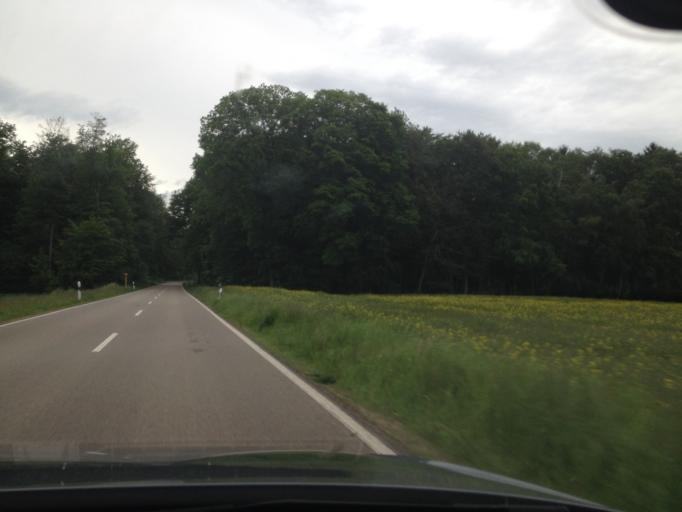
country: DE
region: Saarland
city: Kirkel
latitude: 49.3062
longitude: 7.1988
